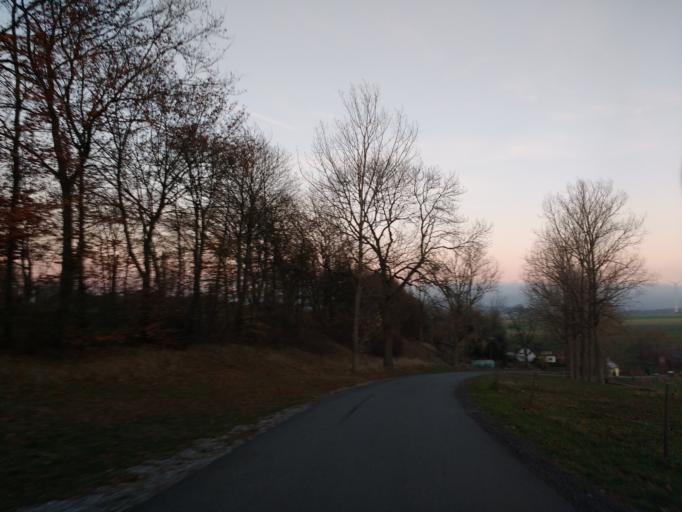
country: DE
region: North Rhine-Westphalia
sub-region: Regierungsbezirk Detmold
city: Paderborn
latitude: 51.6924
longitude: 8.7908
